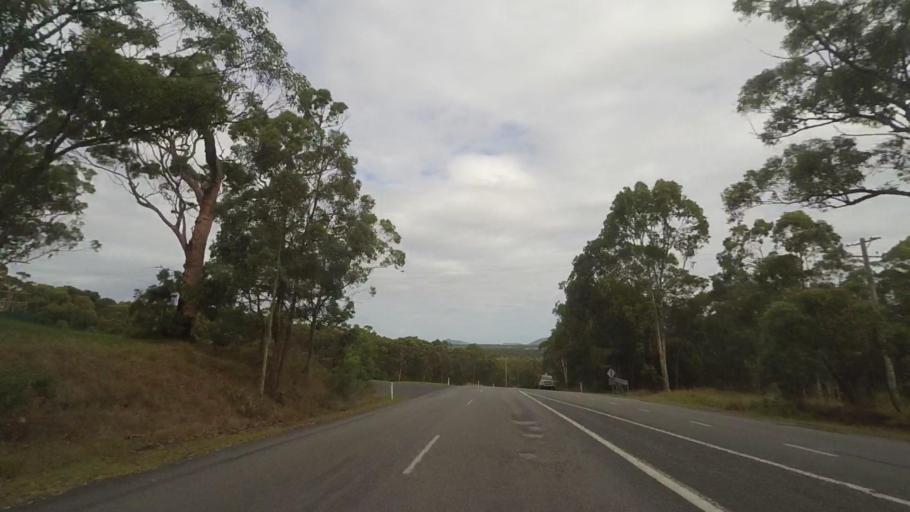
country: AU
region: New South Wales
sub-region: Great Lakes
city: Hawks Nest
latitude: -32.6401
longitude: 152.1441
